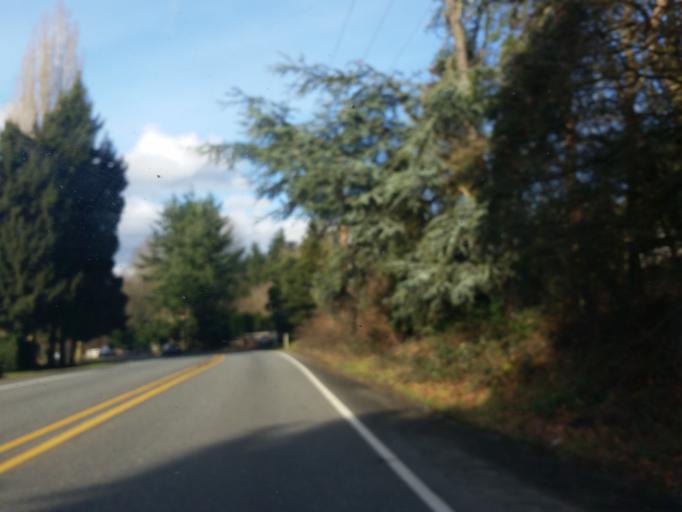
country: US
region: Washington
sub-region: King County
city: Woodinville
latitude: 47.7248
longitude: -122.1357
